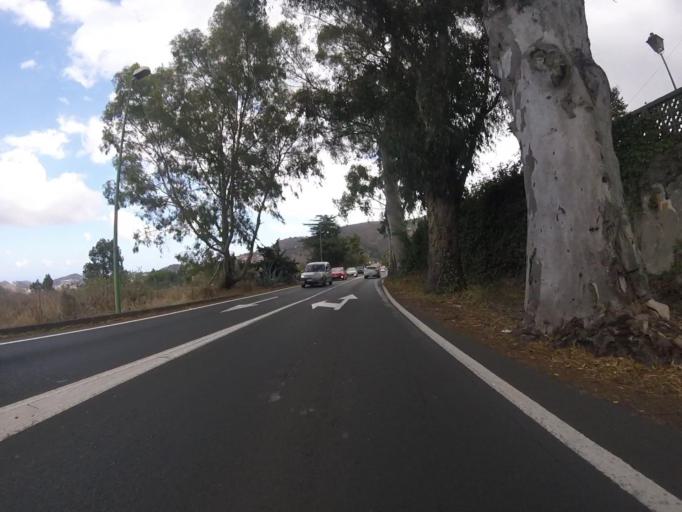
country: ES
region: Canary Islands
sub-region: Provincia de Las Palmas
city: Santa Brigida
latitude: 28.0280
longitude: -15.5077
